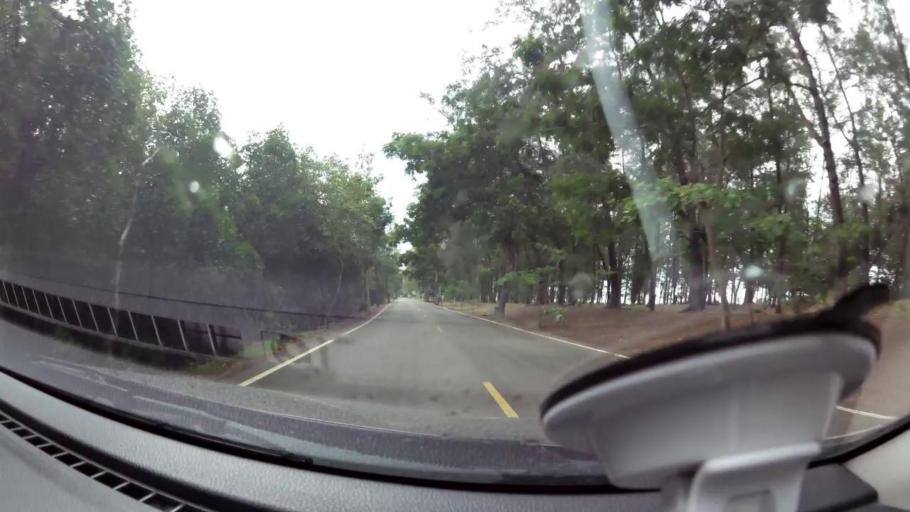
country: TH
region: Prachuap Khiri Khan
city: Pran Buri
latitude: 12.4163
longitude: 99.9846
